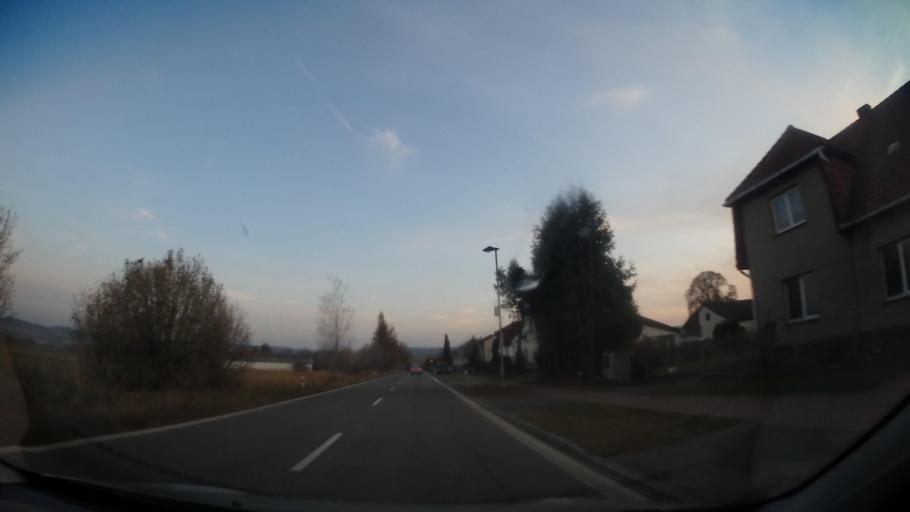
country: CZ
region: Vysocina
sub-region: Okres Pelhrimov
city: Zeliv
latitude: 49.5171
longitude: 15.1752
